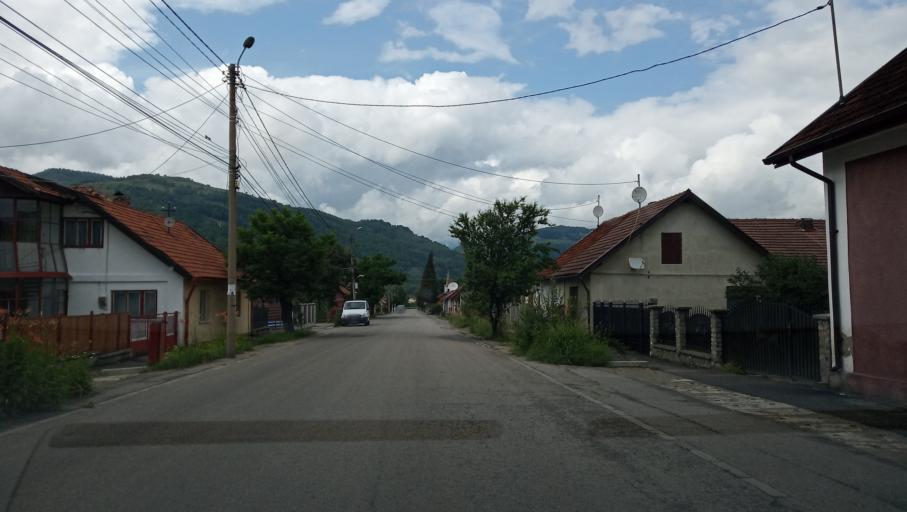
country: RO
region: Hunedoara
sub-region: Oras Petrila
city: Petrila
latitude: 45.4429
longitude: 23.4118
